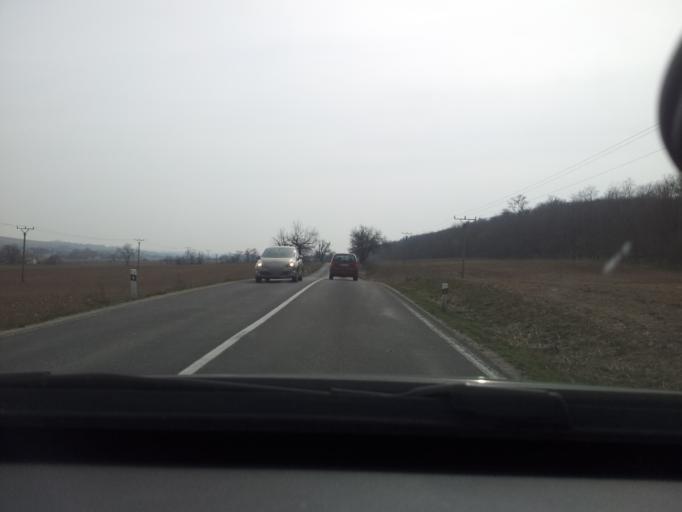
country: SK
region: Trnavsky
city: Hlohovec
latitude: 48.4000
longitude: 17.8476
